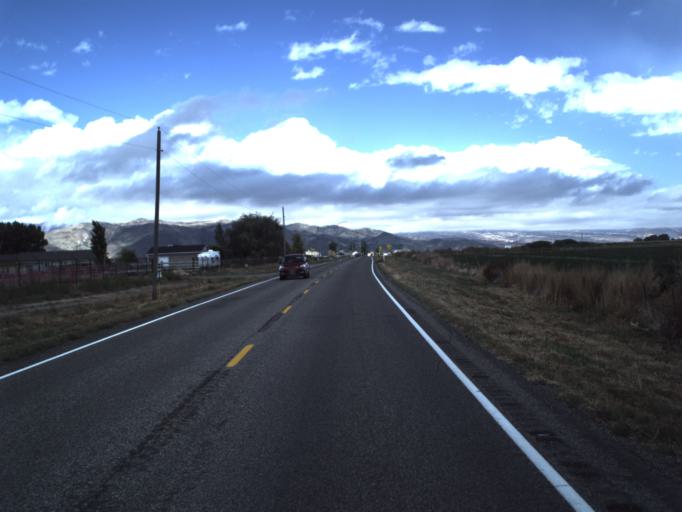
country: US
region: Utah
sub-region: Sevier County
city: Monroe
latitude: 38.6804
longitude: -112.1216
